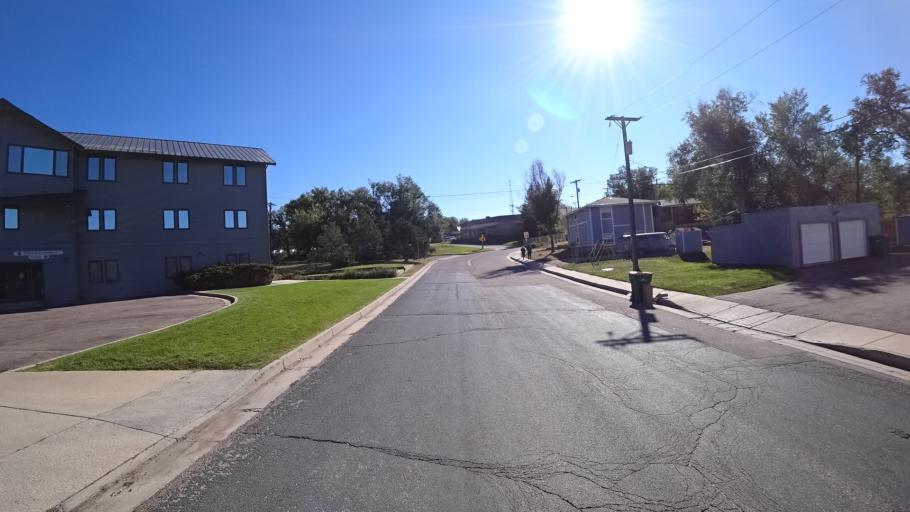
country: US
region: Colorado
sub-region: El Paso County
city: Colorado Springs
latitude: 38.8471
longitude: -104.8454
